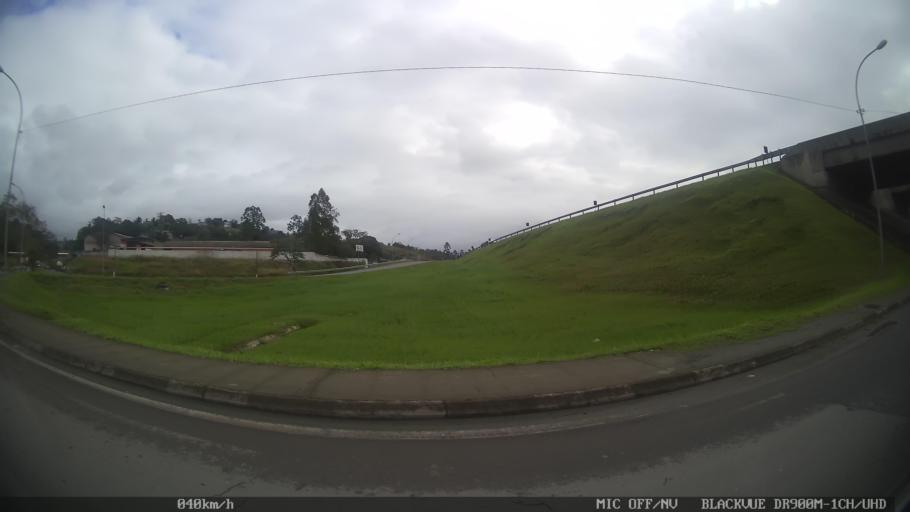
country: BR
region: Sao Paulo
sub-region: Cajati
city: Cajati
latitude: -24.7321
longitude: -48.0987
